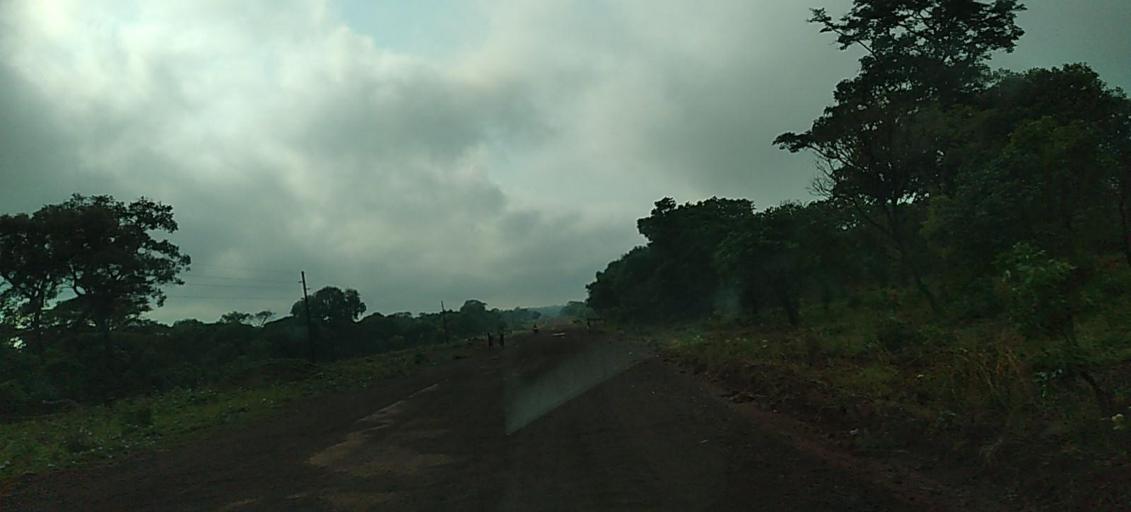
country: ZM
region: North-Western
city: Mwinilunga
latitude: -11.7273
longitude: 24.5781
